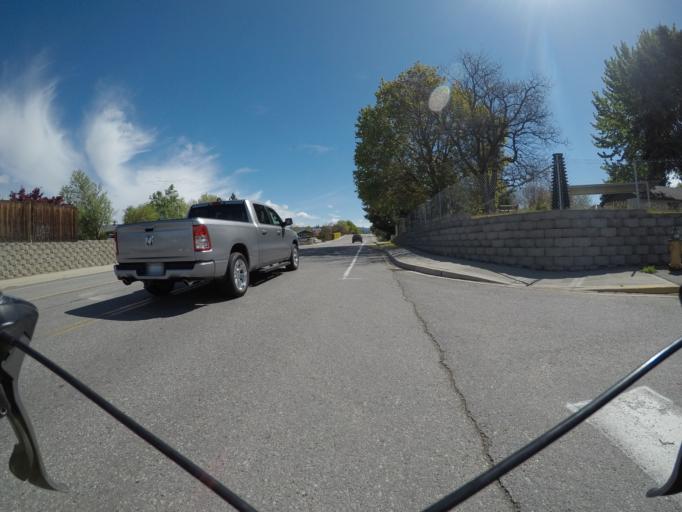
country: US
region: Washington
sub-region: Chelan County
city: South Wenatchee
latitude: 47.3986
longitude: -120.2710
